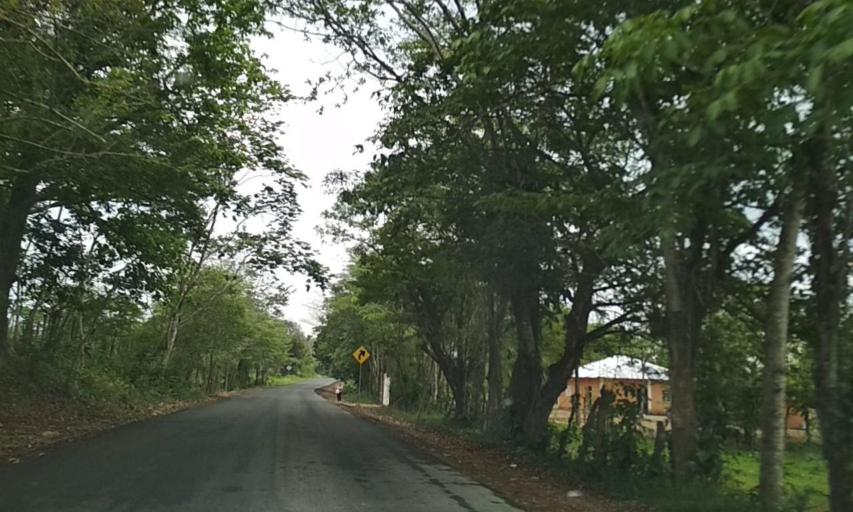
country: MX
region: Tabasco
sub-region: Huimanguillo
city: Francisco Rueda
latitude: 17.6823
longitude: -94.0924
